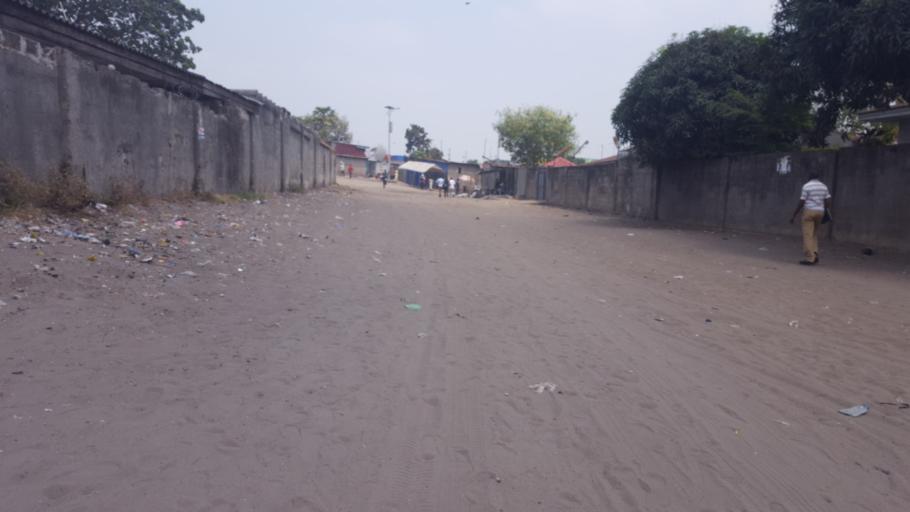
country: CD
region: Kinshasa
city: Masina
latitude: -4.3839
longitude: 15.3538
